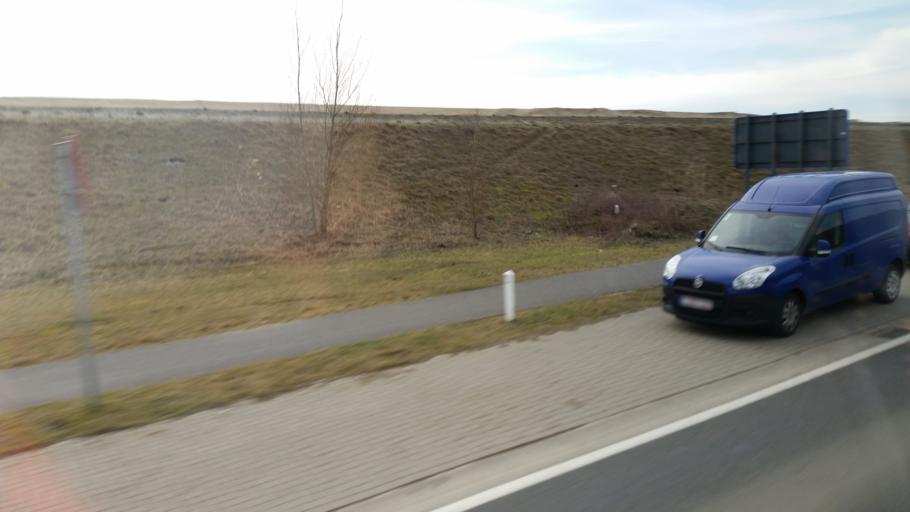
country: BE
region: Flanders
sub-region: Provincie Oost-Vlaanderen
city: Beveren
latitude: 51.3006
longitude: 4.2525
